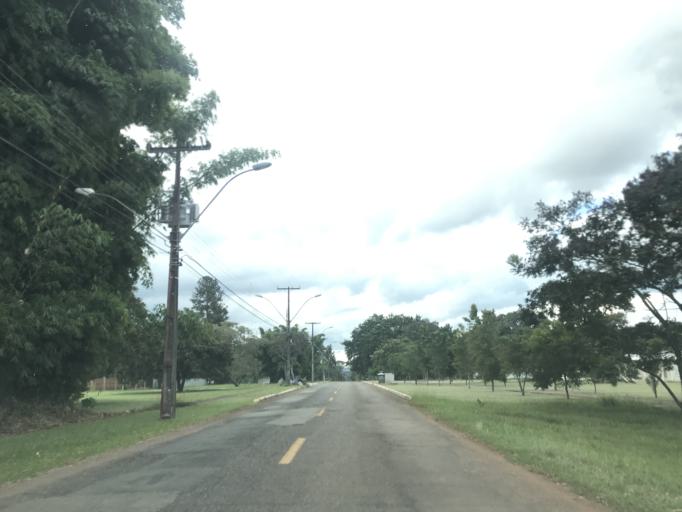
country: BR
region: Federal District
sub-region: Brasilia
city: Brasilia
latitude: -15.9066
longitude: -47.9402
